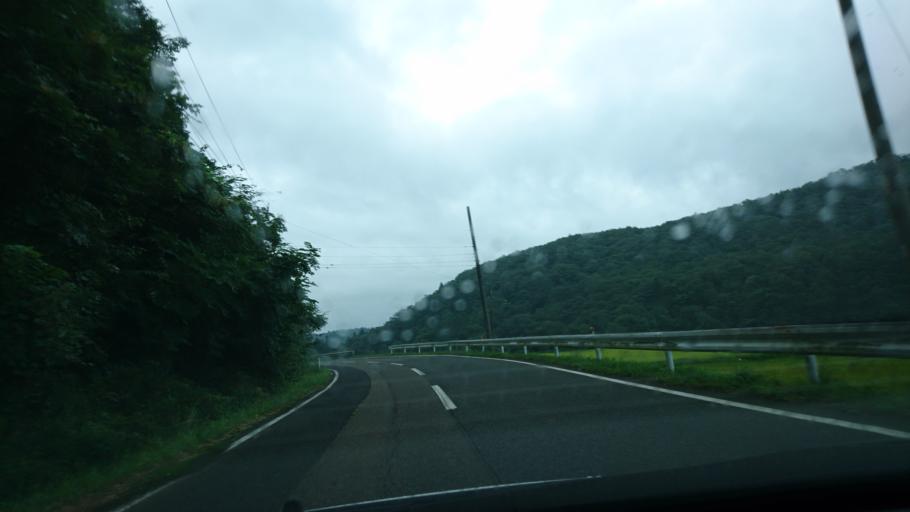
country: JP
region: Iwate
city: Ichinoseki
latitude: 38.9015
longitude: 141.0424
